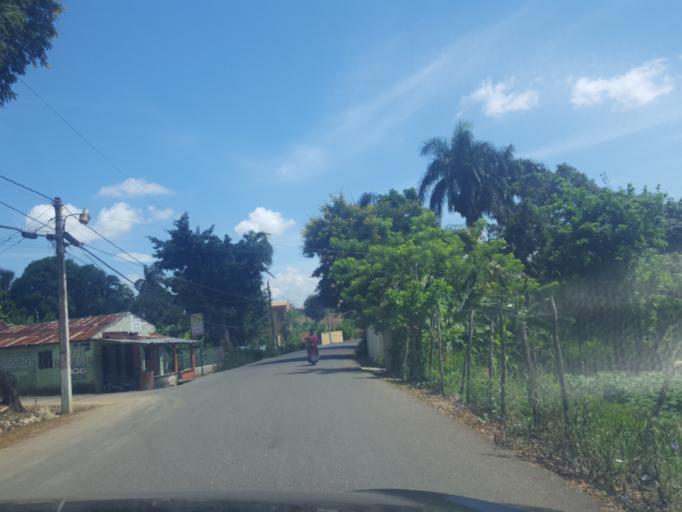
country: DO
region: Santiago
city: Baitoa
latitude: 19.3740
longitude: -70.6523
